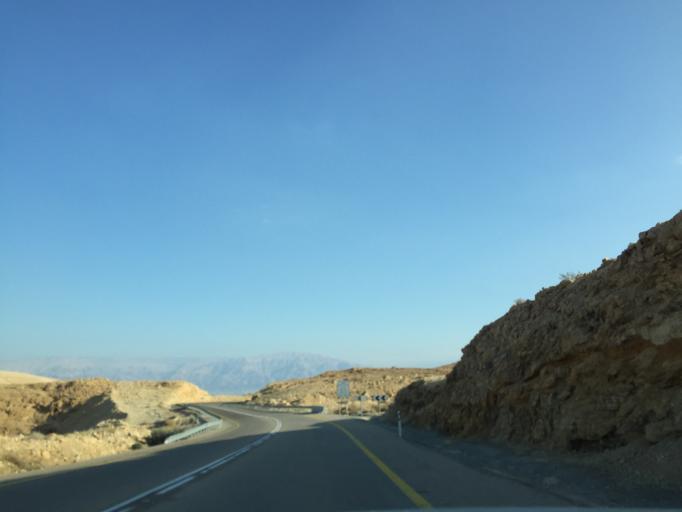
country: IL
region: Southern District
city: `En Boqeq
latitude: 31.1616
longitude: 35.3264
